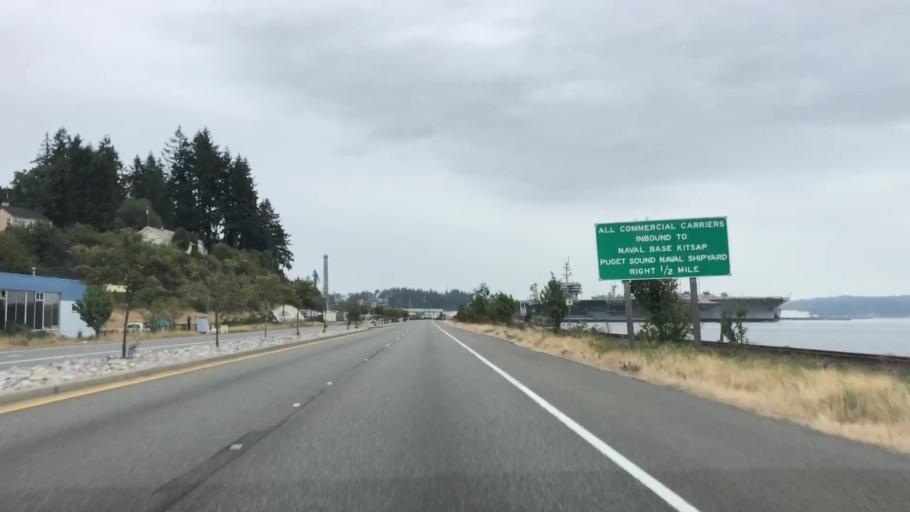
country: US
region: Washington
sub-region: Kitsap County
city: Navy Yard City
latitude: 47.5497
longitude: -122.6661
